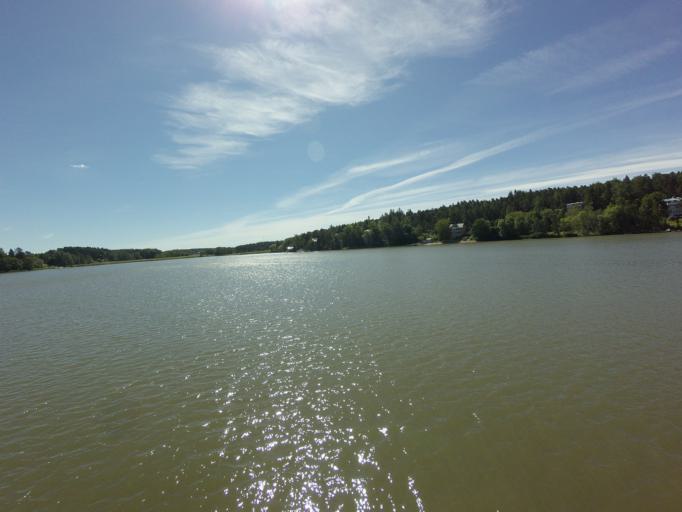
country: FI
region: Varsinais-Suomi
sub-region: Turku
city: Raisio
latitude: 60.4203
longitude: 22.1692
